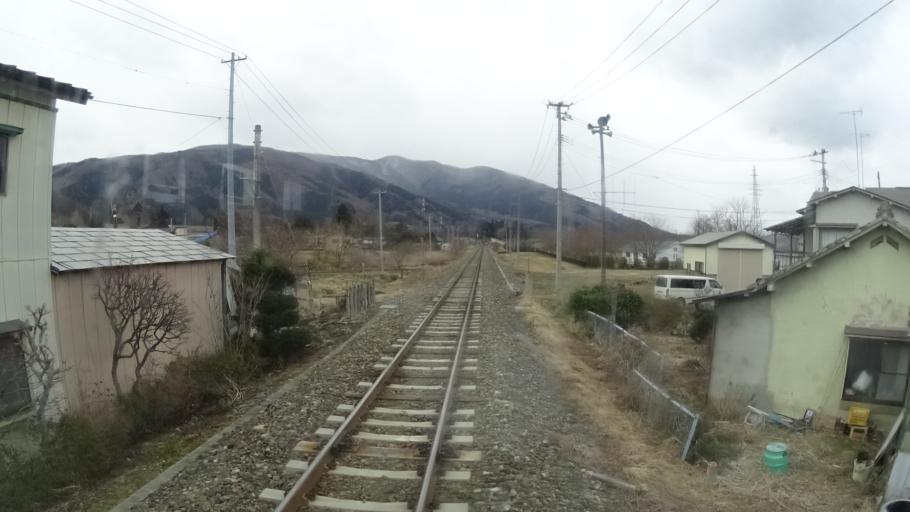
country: JP
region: Iwate
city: Tono
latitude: 39.3325
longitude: 141.5246
